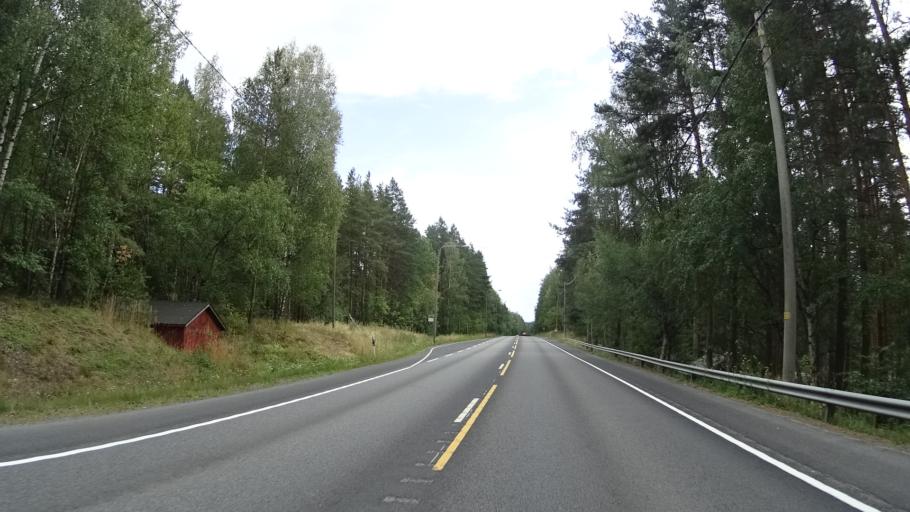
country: FI
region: Pirkanmaa
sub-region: Tampere
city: Kangasala
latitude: 61.4295
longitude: 24.1306
